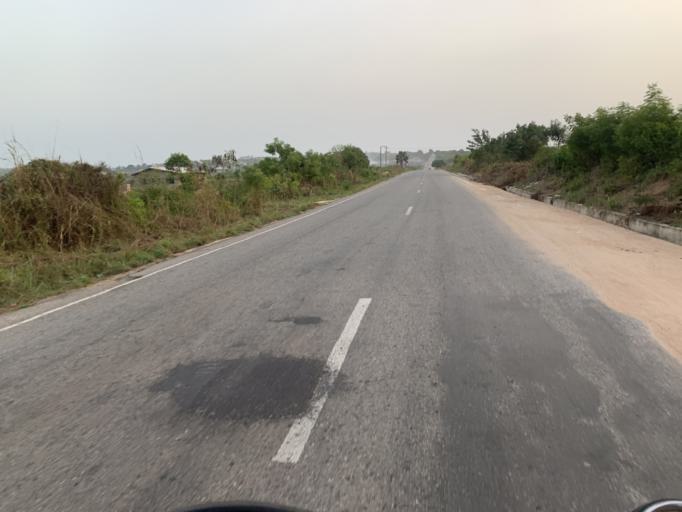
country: GH
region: Central
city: Winneba
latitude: 5.3684
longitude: -0.6078
